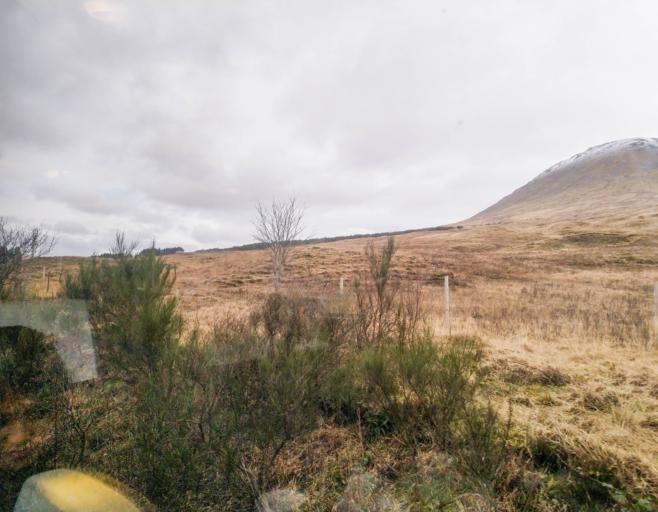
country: GB
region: Scotland
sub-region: Highland
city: Spean Bridge
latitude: 56.5138
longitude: -4.7624
